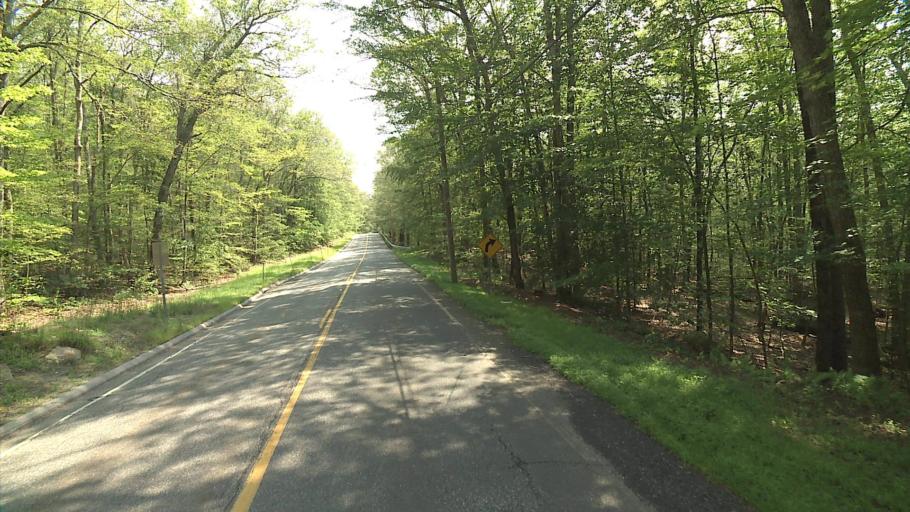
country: US
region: Connecticut
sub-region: New London County
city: Montville Center
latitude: 41.5022
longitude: -72.1773
